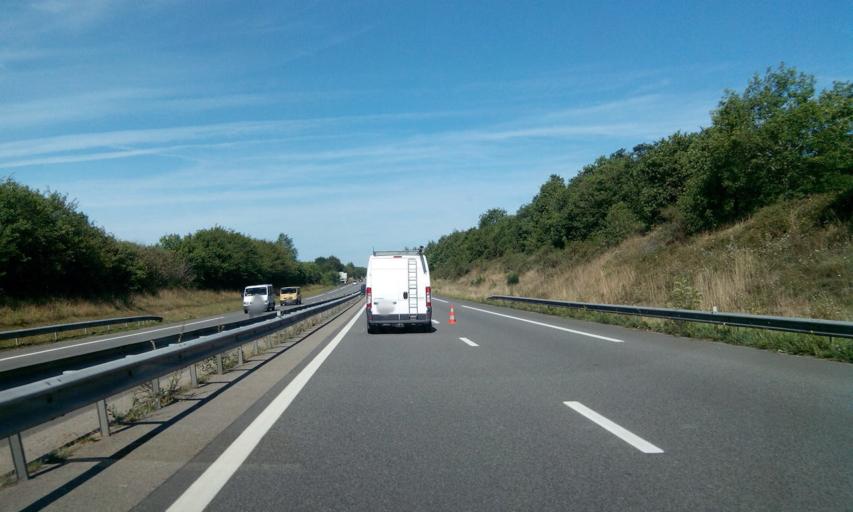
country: FR
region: Limousin
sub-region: Departement de la Haute-Vienne
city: Saint-Victurnien
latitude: 45.8898
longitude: 1.0556
